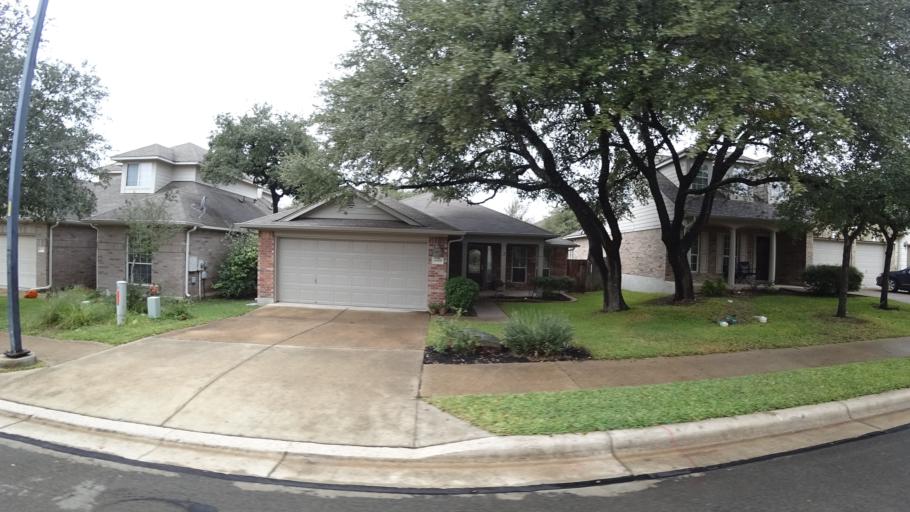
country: US
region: Texas
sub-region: Travis County
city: Shady Hollow
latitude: 30.1905
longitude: -97.8682
